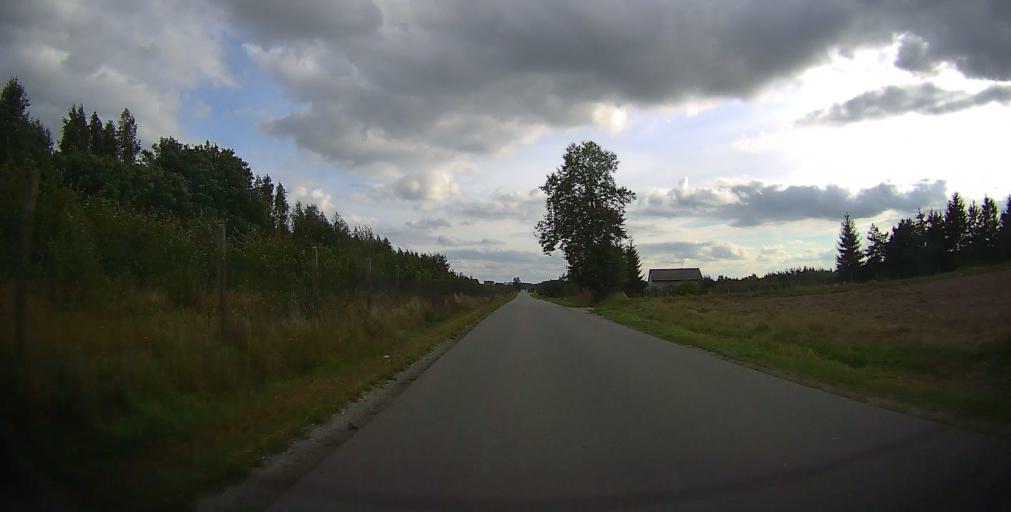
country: PL
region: Masovian Voivodeship
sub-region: Powiat bialobrzeski
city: Promna
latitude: 51.7176
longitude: 20.9584
